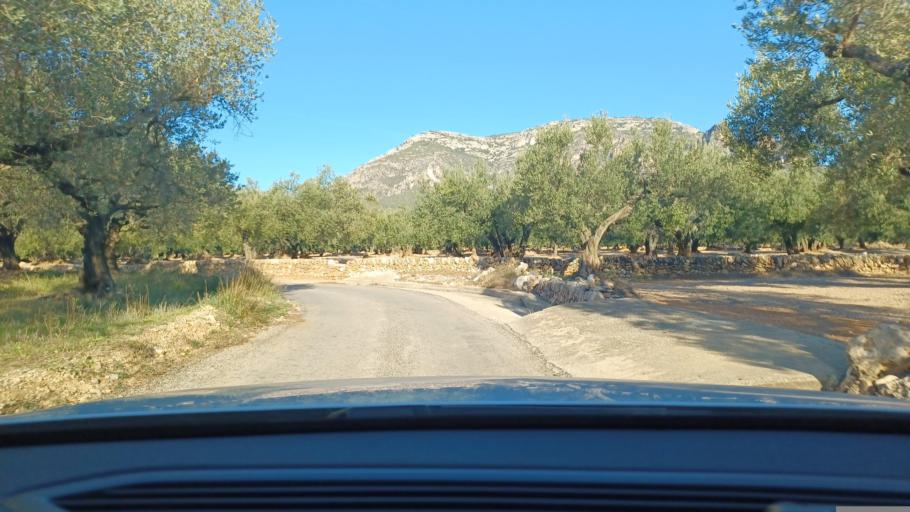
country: ES
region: Catalonia
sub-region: Provincia de Tarragona
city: Mas de Barberans
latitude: 40.7168
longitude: 0.3581
